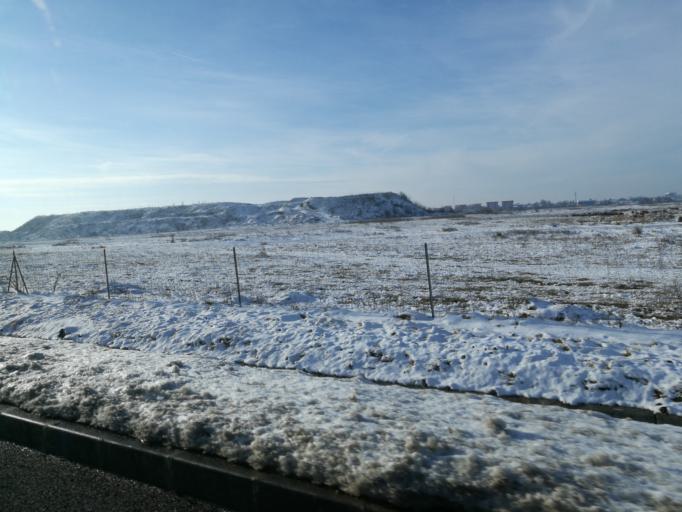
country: RO
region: Ilfov
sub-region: Voluntari City
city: Voluntari
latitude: 44.5005
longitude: 26.1542
